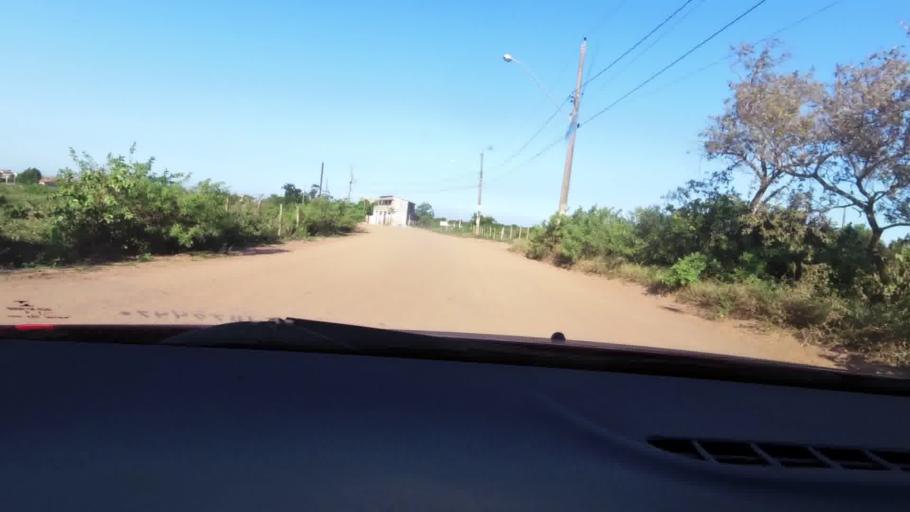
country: BR
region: Espirito Santo
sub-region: Guarapari
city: Guarapari
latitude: -20.5551
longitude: -40.4105
